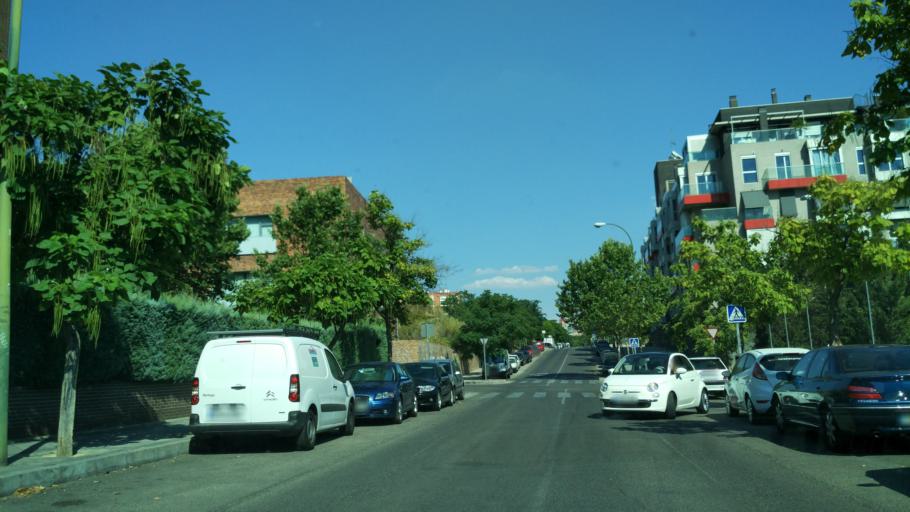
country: ES
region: Madrid
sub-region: Provincia de Madrid
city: Tetuan de las Victorias
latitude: 40.4722
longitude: -3.7187
